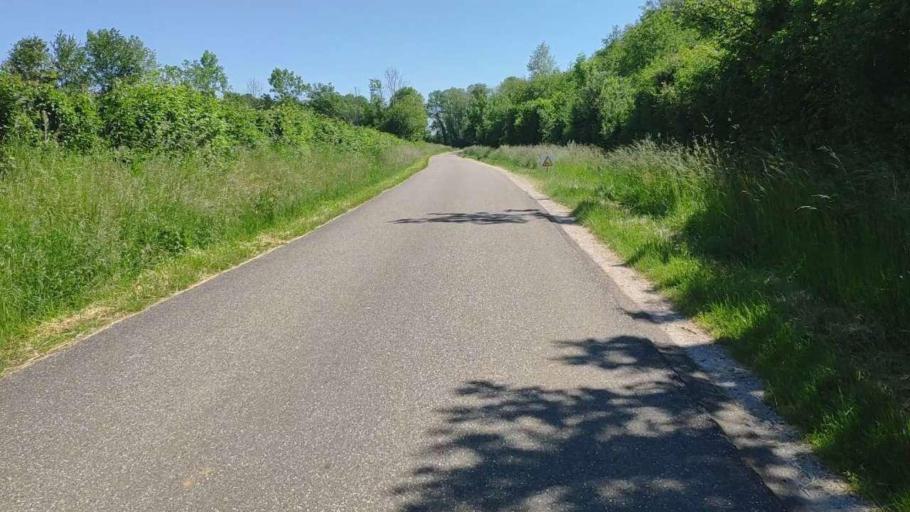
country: FR
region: Franche-Comte
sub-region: Departement du Jura
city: Bletterans
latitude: 46.7631
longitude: 5.4233
